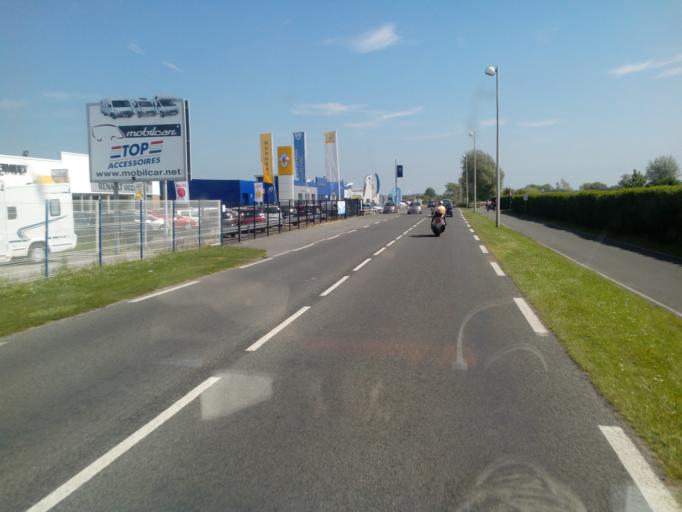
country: FR
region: Nord-Pas-de-Calais
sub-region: Departement du Pas-de-Calais
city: Berck
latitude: 50.4001
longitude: 1.5981
